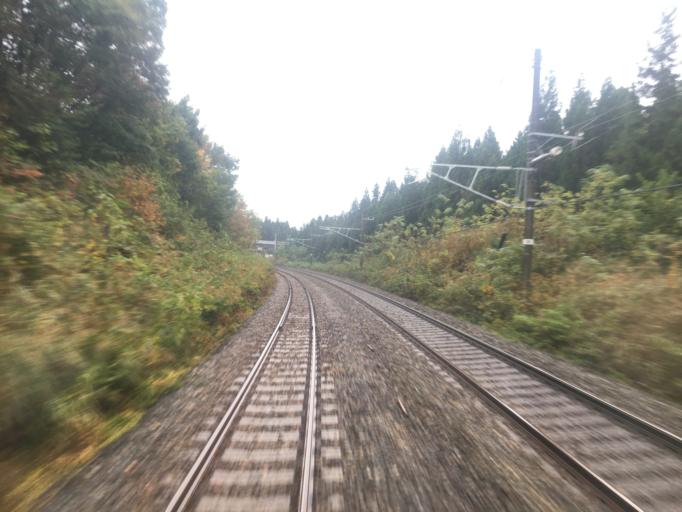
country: JP
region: Yamagata
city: Shinjo
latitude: 38.7329
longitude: 140.3074
